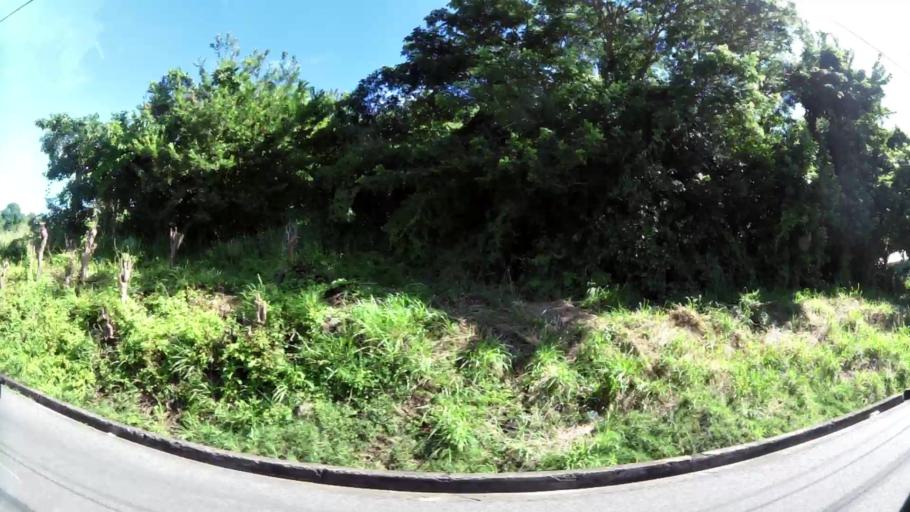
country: TT
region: Tobago
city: Scarborough
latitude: 11.1757
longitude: -60.7300
